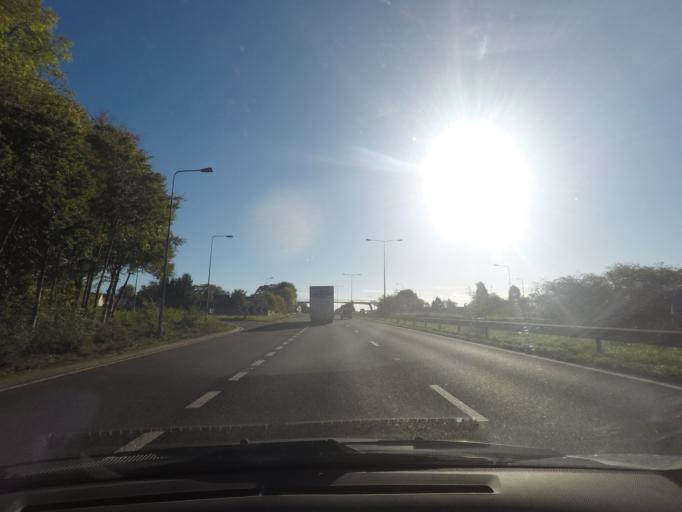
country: GB
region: England
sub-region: East Riding of Yorkshire
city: Welton
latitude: 53.7318
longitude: -0.5536
